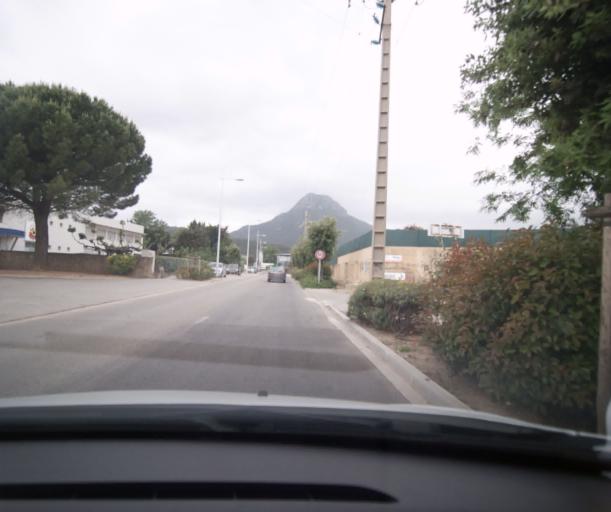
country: FR
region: Provence-Alpes-Cote d'Azur
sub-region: Departement du Var
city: La Farlede
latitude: 43.1483
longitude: 6.0390
